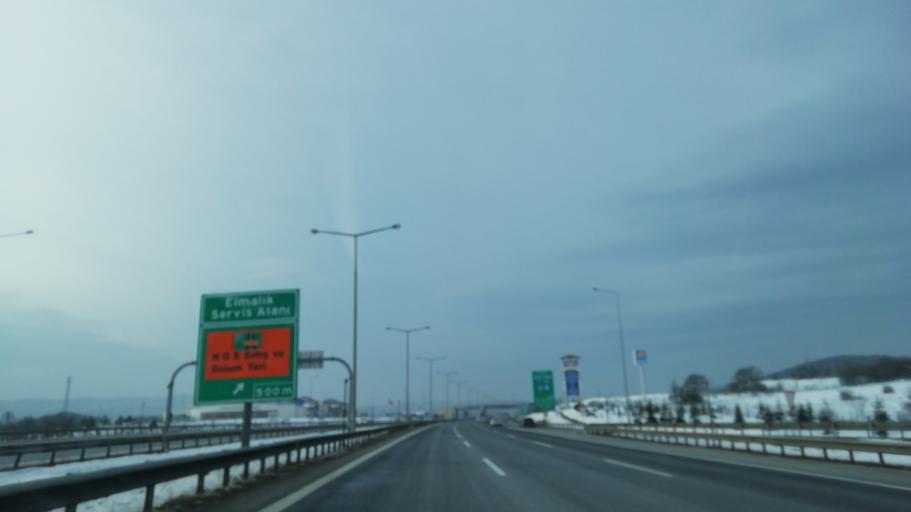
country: TR
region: Bolu
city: Bolu
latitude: 40.7223
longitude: 31.4742
